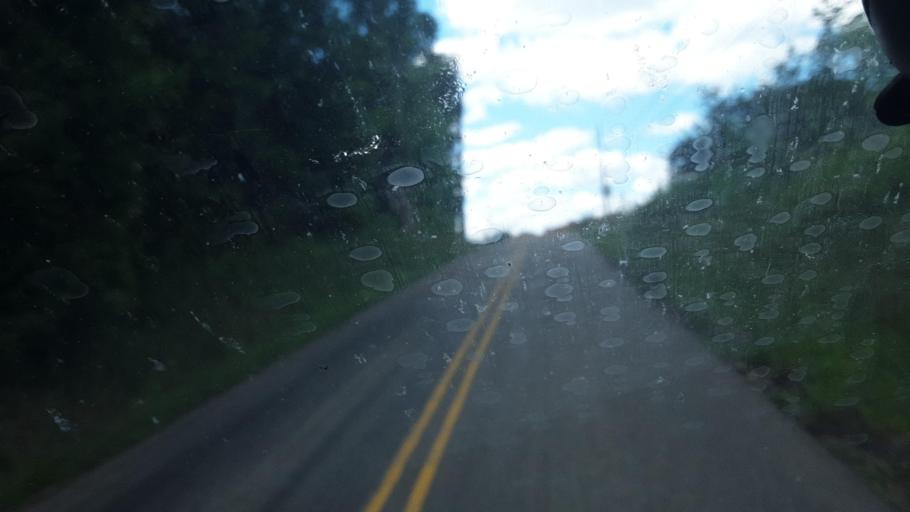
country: US
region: Pennsylvania
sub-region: Lawrence County
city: New Wilmington
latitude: 41.0650
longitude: -80.2466
